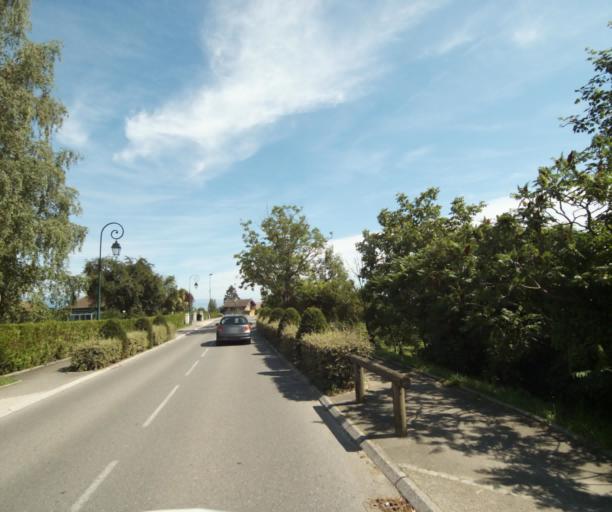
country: FR
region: Rhone-Alpes
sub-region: Departement de la Haute-Savoie
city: Margencel
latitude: 46.3391
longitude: 6.4331
